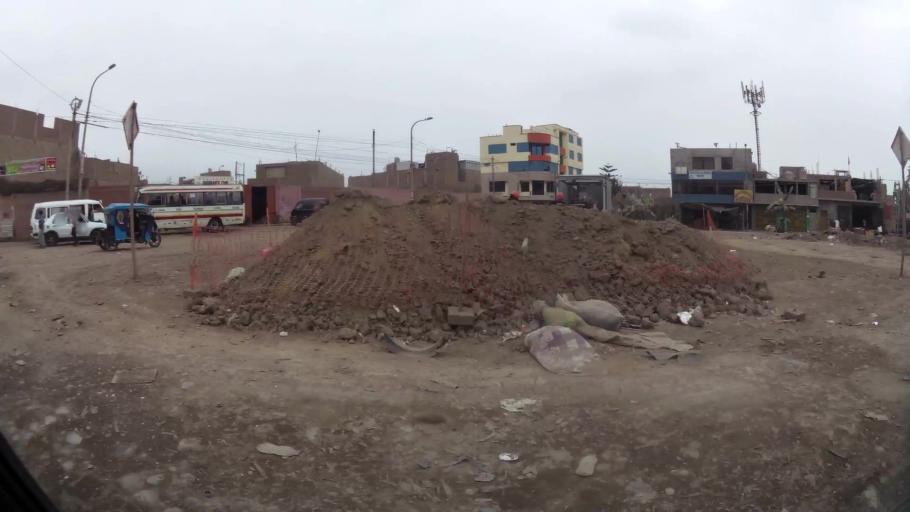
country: PE
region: Lima
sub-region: Lima
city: Independencia
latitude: -11.9559
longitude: -77.0889
